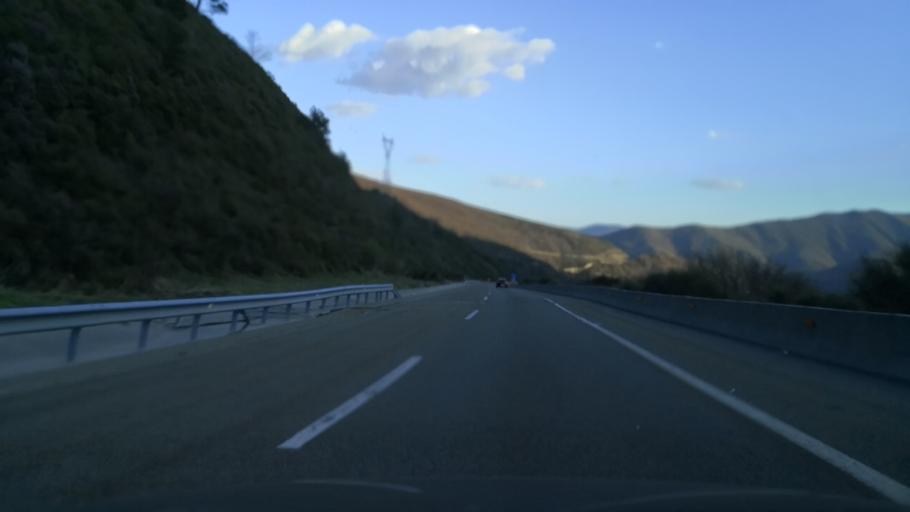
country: ES
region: Castille and Leon
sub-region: Provincia de Leon
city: Vega de Valcarce
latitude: 42.6961
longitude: -6.9963
